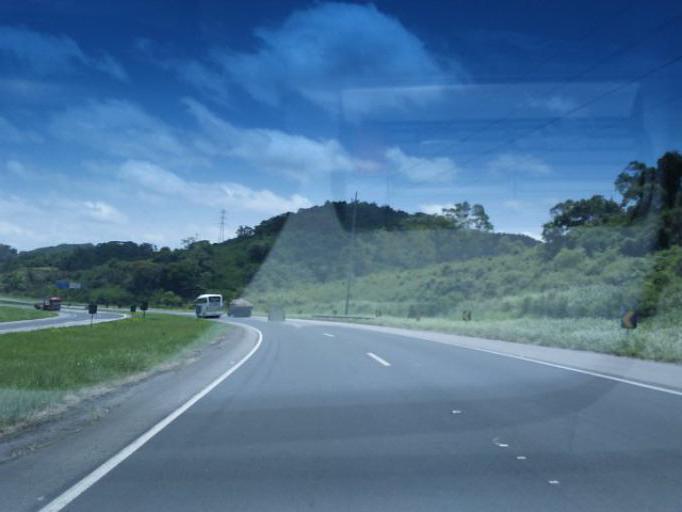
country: BR
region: Sao Paulo
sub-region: Juquia
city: Juquia
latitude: -24.3715
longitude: -47.7054
